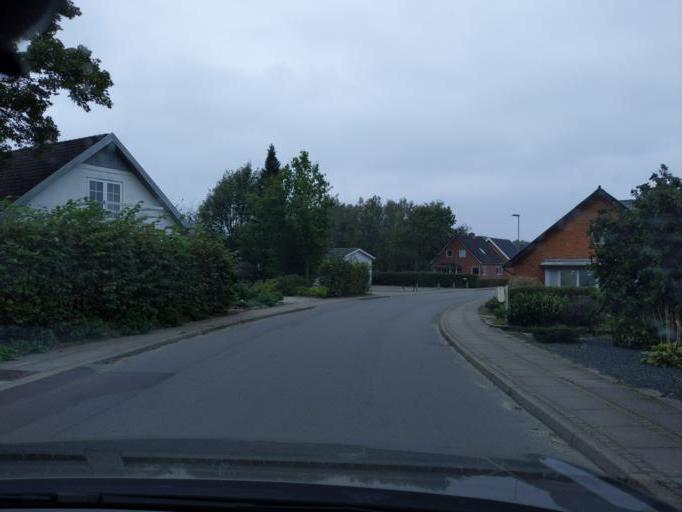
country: DK
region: Central Jutland
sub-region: Viborg Kommune
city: Stoholm
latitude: 56.4760
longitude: 9.2283
